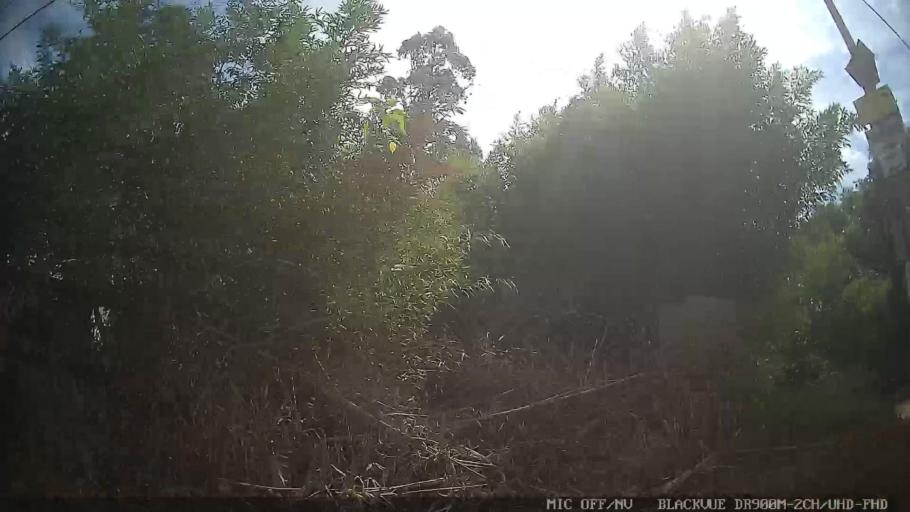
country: BR
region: Sao Paulo
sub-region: Jarinu
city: Jarinu
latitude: -23.0080
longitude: -46.6559
